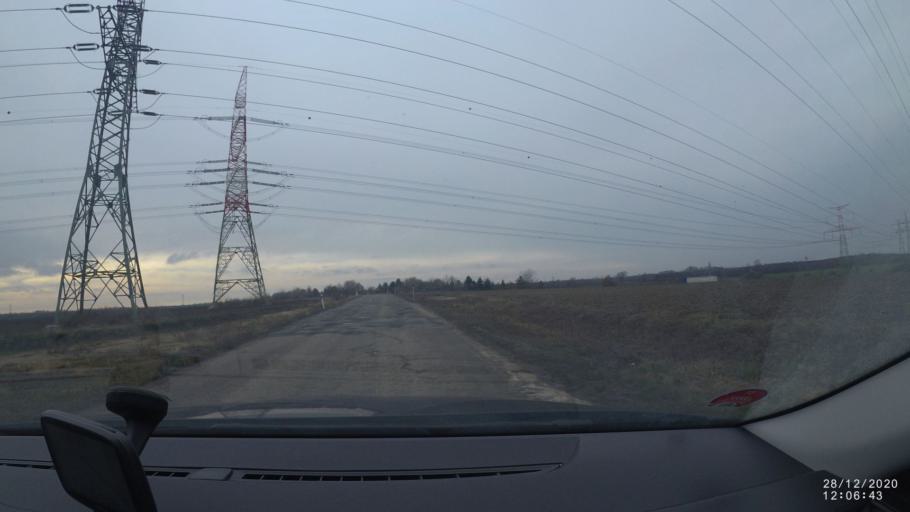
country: CZ
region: Central Bohemia
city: Zelenec
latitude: 50.1599
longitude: 14.6670
